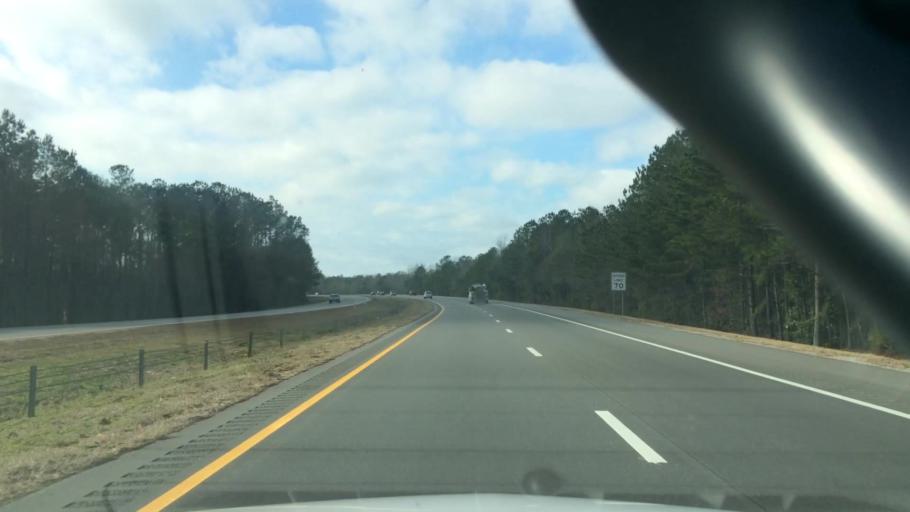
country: US
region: North Carolina
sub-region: New Hanover County
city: Wrightsboro
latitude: 34.3189
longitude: -77.9299
